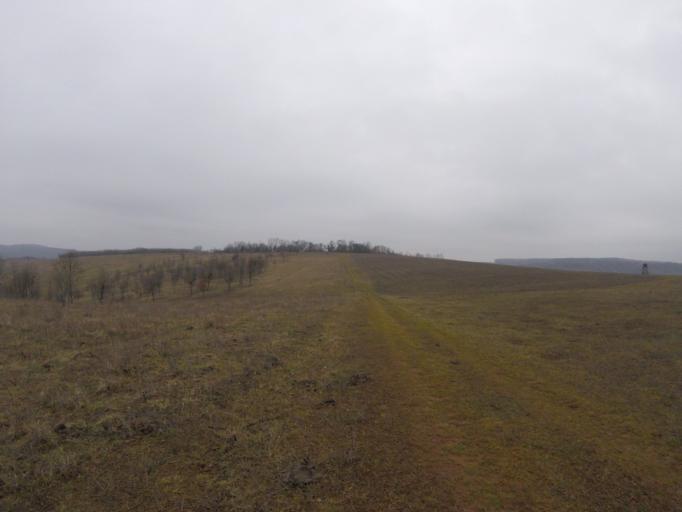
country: HU
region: Borsod-Abauj-Zemplen
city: Rudabanya
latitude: 48.4471
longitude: 20.5940
